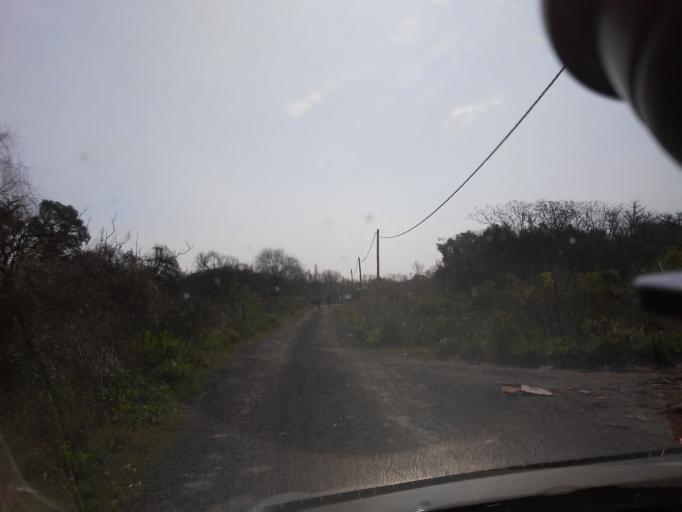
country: AR
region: Buenos Aires
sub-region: Partido de Avellaneda
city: Avellaneda
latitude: -34.6678
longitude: -58.3134
